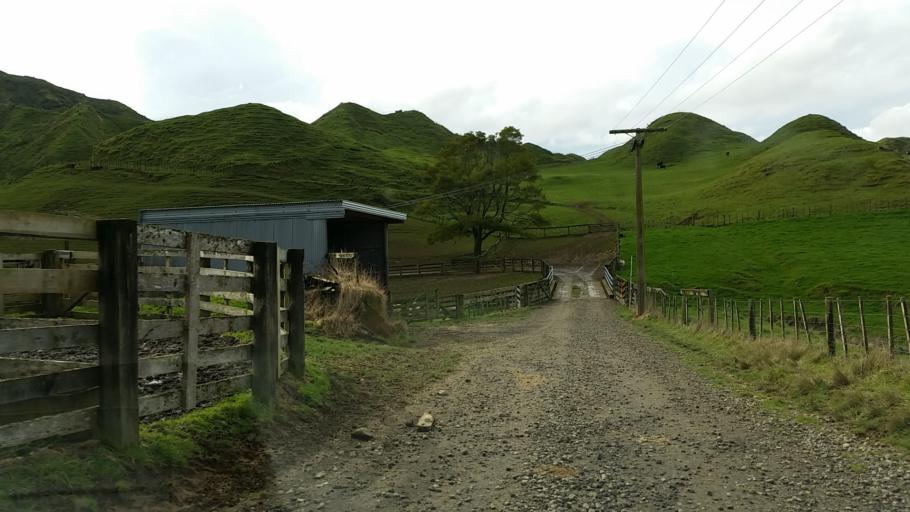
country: NZ
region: Taranaki
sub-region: South Taranaki District
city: Eltham
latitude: -39.4114
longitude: 174.4482
